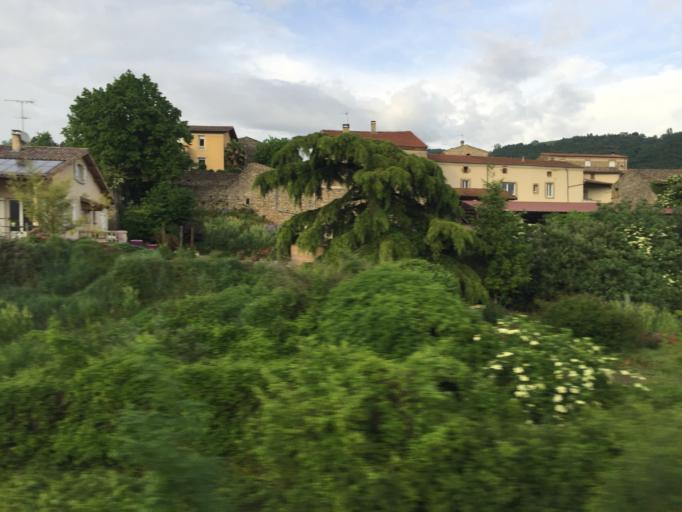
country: FR
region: Rhone-Alpes
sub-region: Departement de l'Ardeche
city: Saint-Jean-de-Muzols
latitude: 45.1076
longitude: 4.8299
